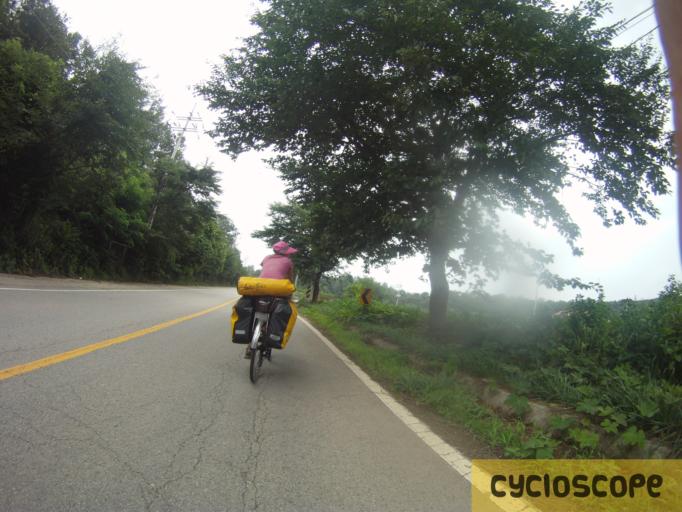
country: KR
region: Gyeonggi-do
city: Hwaseong-si
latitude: 37.1416
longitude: 126.8671
